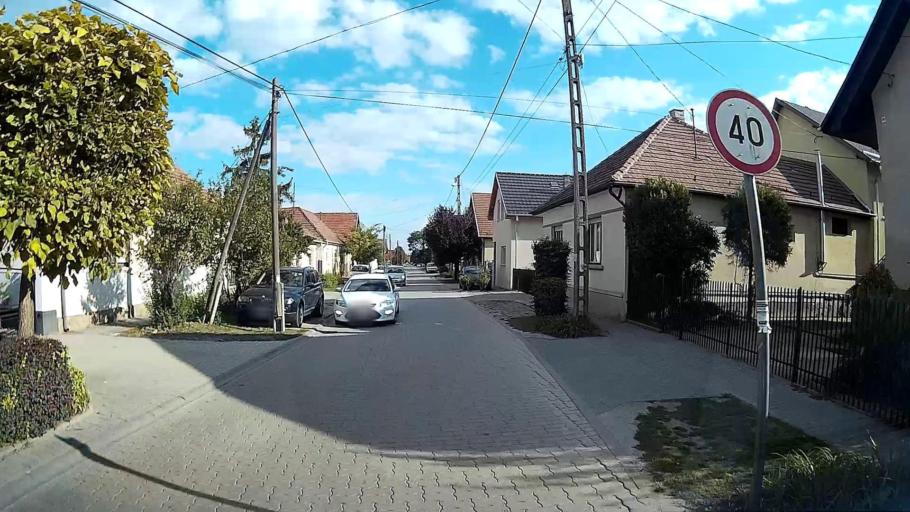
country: HU
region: Pest
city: Pilisvorosvar
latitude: 47.6245
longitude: 18.9023
